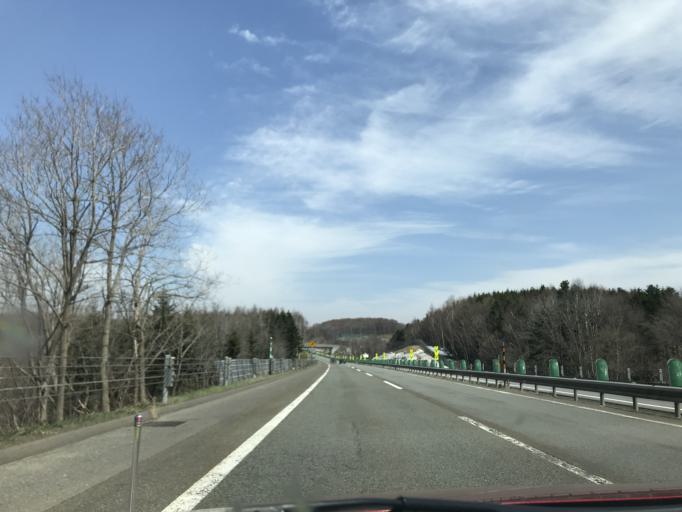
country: JP
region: Hokkaido
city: Iwamizawa
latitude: 43.1992
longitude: 141.8087
